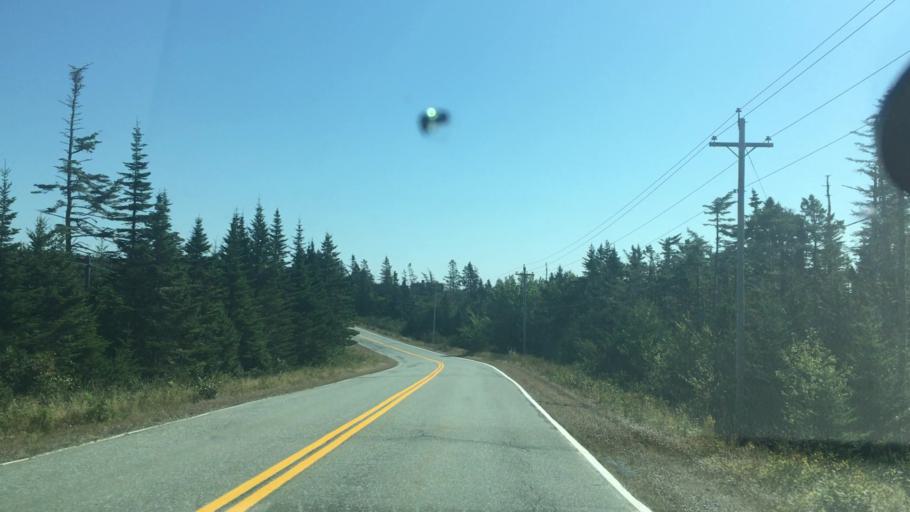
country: CA
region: Nova Scotia
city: New Glasgow
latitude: 44.9173
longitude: -62.3290
